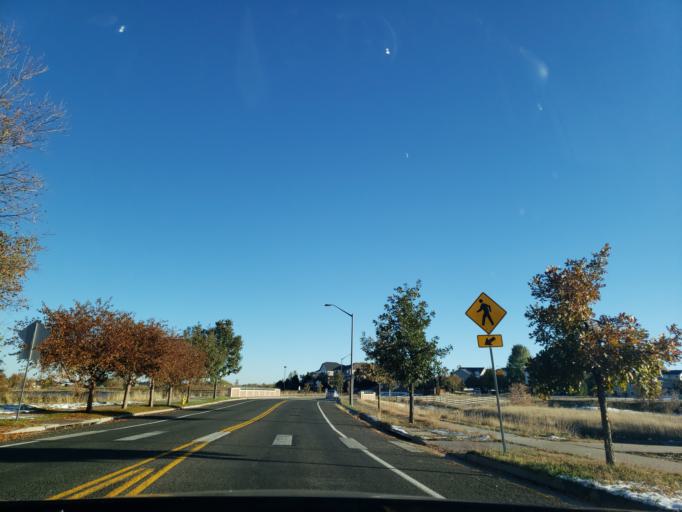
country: US
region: Colorado
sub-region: Larimer County
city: Fort Collins
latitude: 40.5081
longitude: -105.0674
